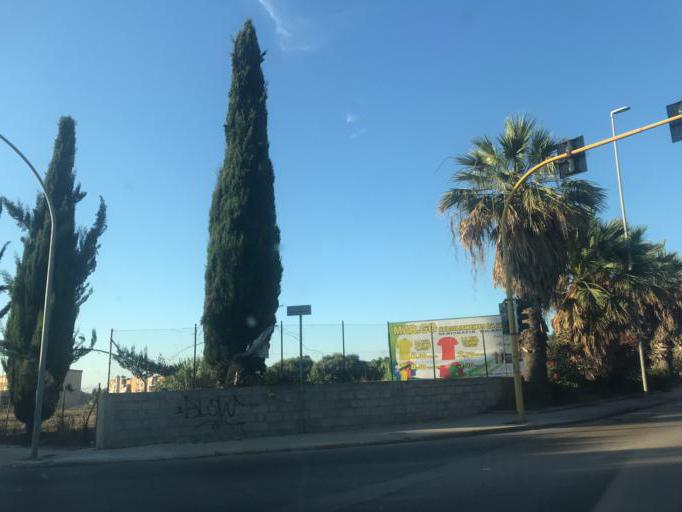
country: IT
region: Sardinia
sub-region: Provincia di Sassari
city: Alghero
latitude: 40.5657
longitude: 8.3310
